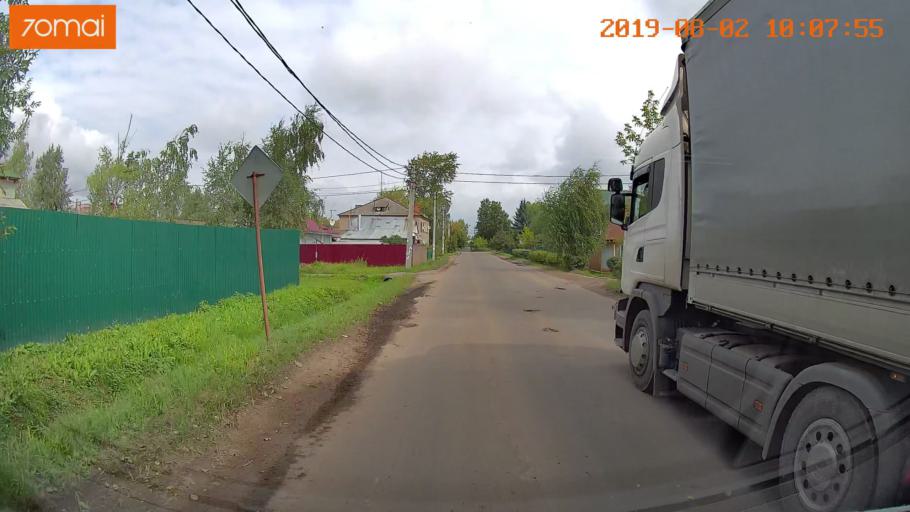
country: RU
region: Ivanovo
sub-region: Gorod Ivanovo
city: Ivanovo
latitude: 56.9842
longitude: 40.9366
